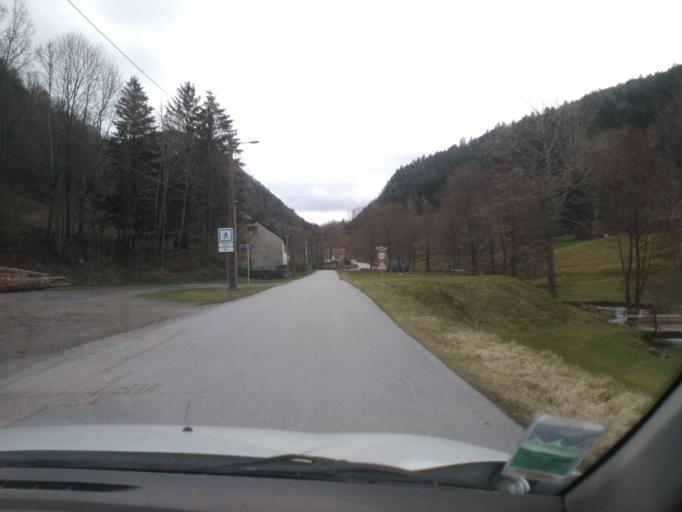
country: FR
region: Lorraine
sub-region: Departement des Vosges
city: Bussang
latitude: 47.8894
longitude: 6.8825
